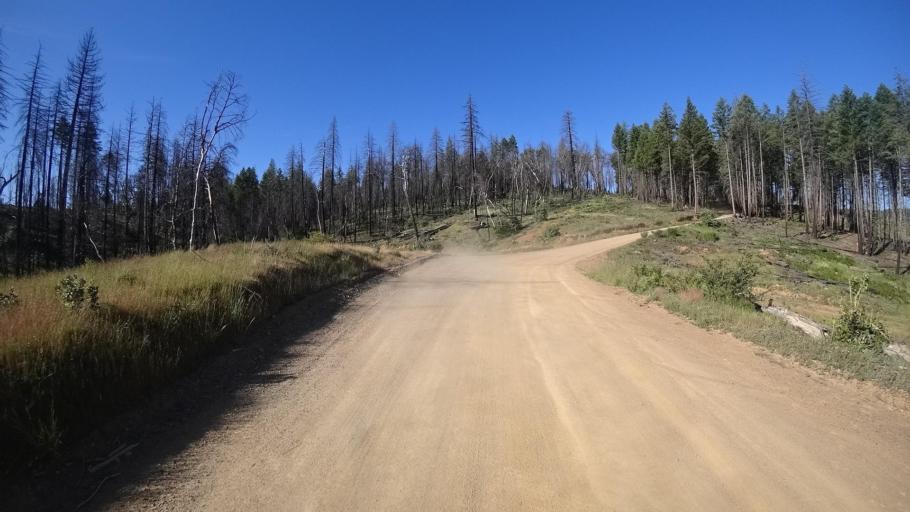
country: US
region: California
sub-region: Lake County
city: Upper Lake
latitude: 39.3867
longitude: -122.9811
